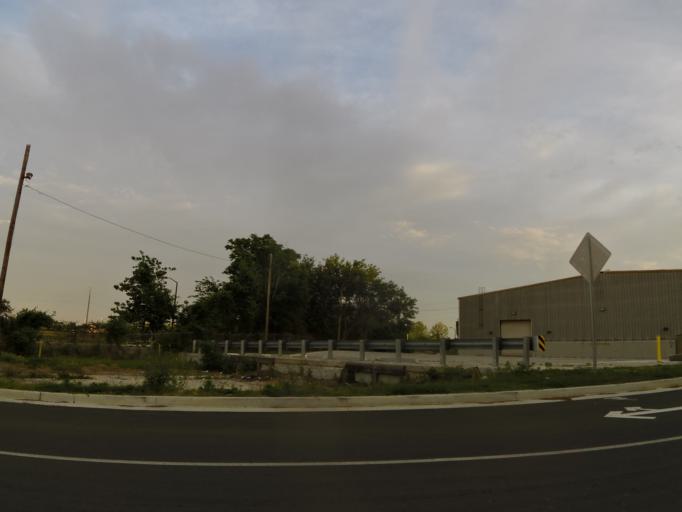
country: US
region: Georgia
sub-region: Chatham County
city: Savannah
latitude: 32.0769
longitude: -81.0821
